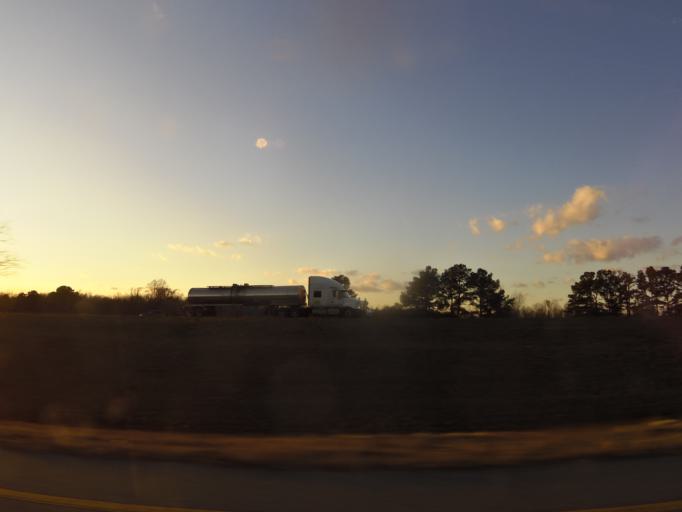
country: US
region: North Carolina
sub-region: Robeson County
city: Rowland
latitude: 34.5025
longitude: -79.3062
